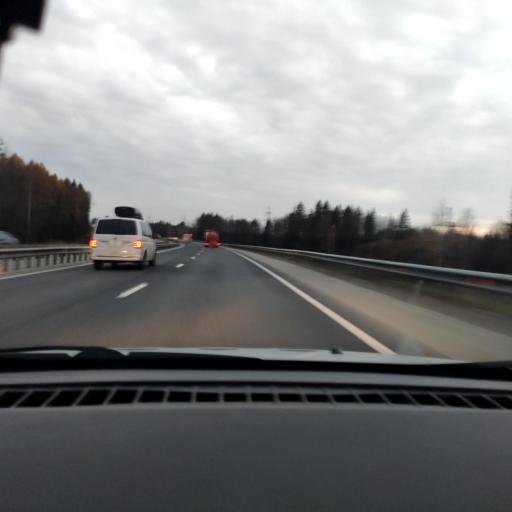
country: RU
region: Perm
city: Ferma
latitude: 58.0140
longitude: 56.4054
